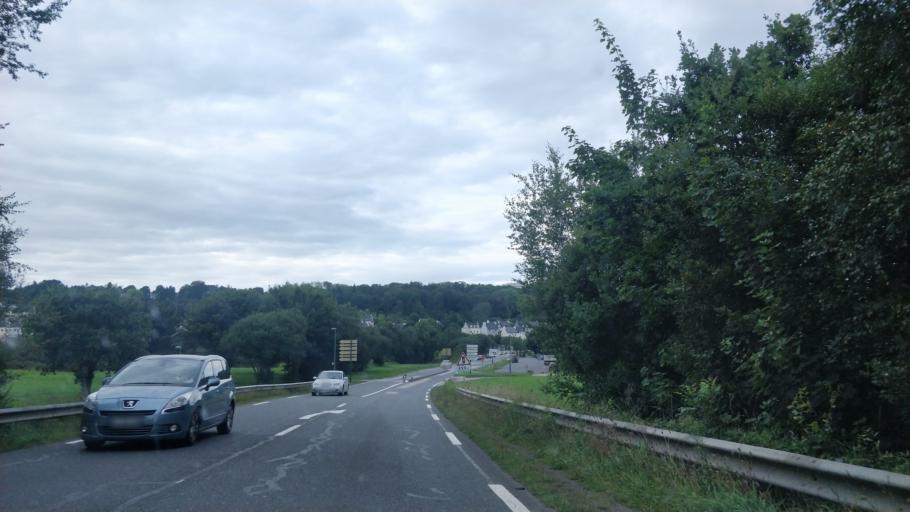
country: FR
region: Brittany
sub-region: Departement du Finistere
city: Landerneau
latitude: 48.4421
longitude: -4.2679
